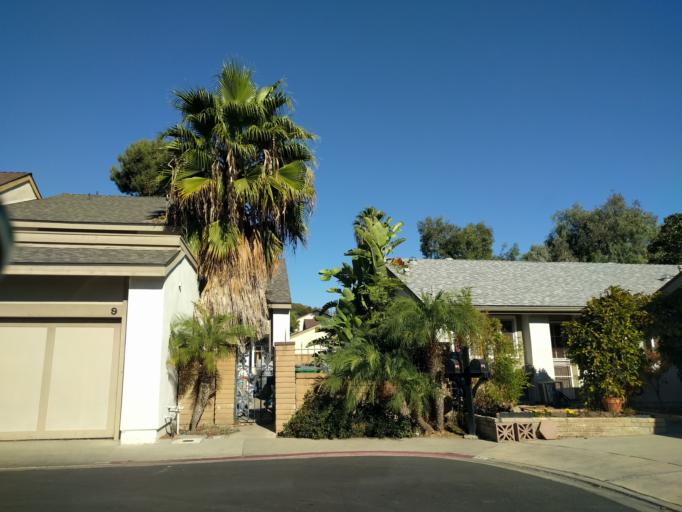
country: US
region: California
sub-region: Orange County
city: Irvine
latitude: 33.7062
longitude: -117.7823
